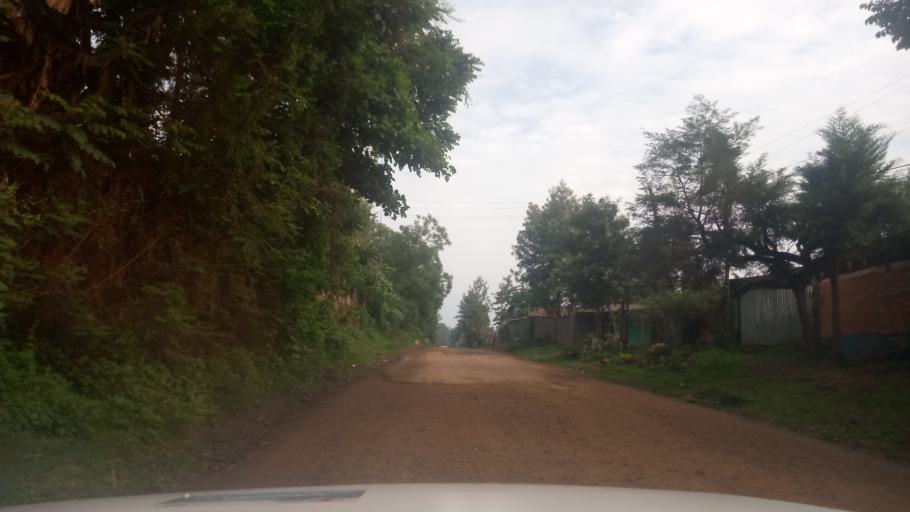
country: ET
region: Oromiya
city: Agaro
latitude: 7.8406
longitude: 36.6629
